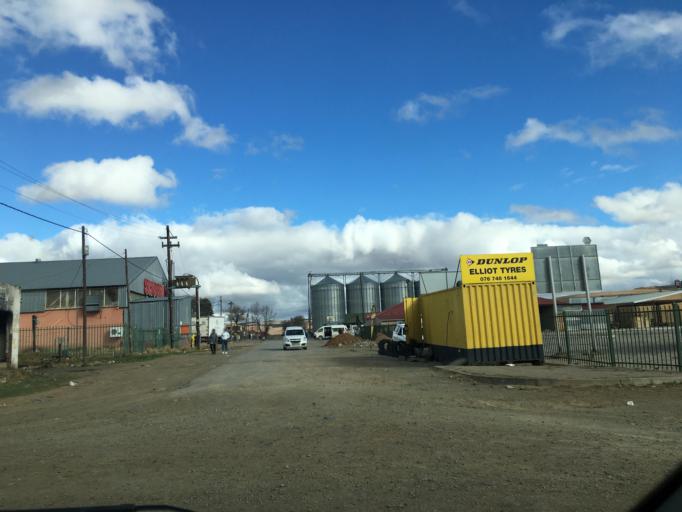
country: ZA
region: Eastern Cape
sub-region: Chris Hani District Municipality
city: Elliot
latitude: -31.3338
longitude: 27.8465
